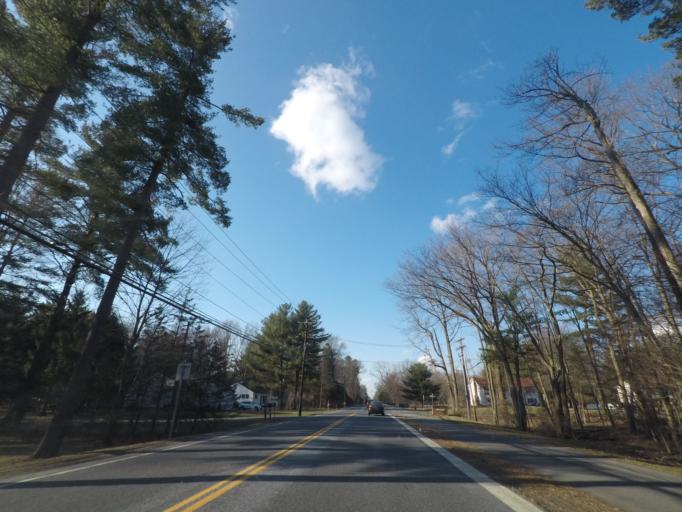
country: US
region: New York
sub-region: Saratoga County
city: Country Knolls
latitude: 42.8433
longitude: -73.7941
